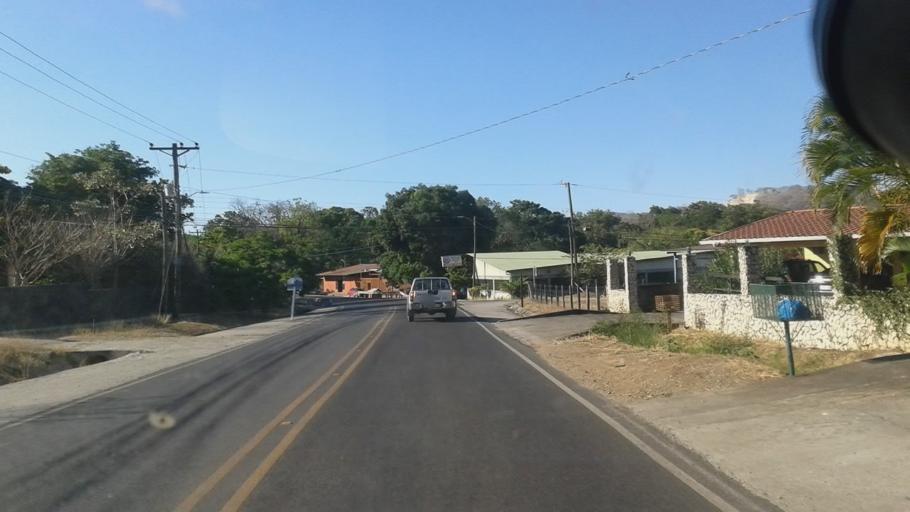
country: CR
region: Guanacaste
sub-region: Canton de Nicoya
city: Nicoya
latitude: 10.1353
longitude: -85.4463
